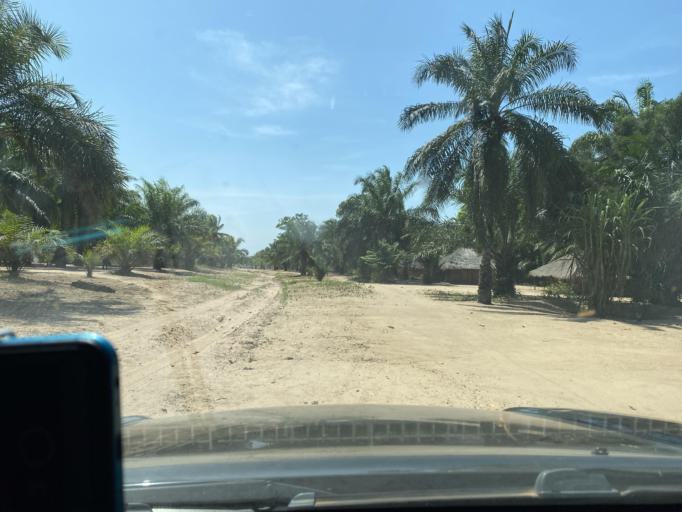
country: CD
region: Kasai-Oriental
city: Kabinda
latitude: -5.9165
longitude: 24.8498
